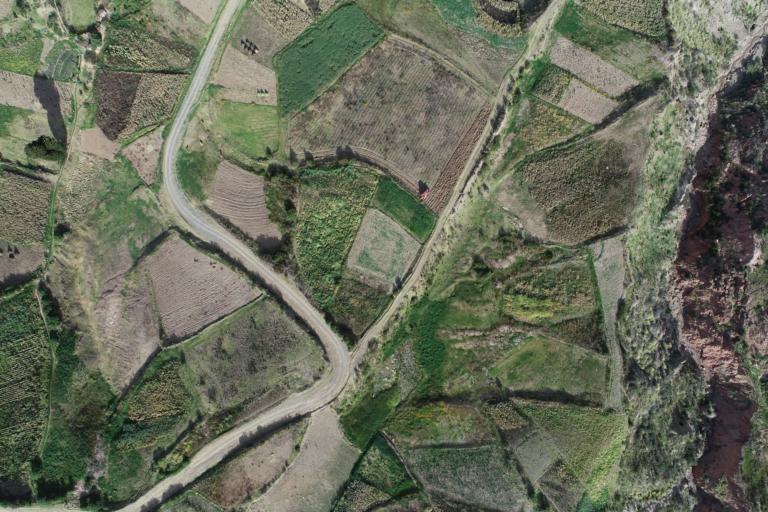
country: BO
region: La Paz
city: La Paz
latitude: -16.5535
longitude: -67.9906
